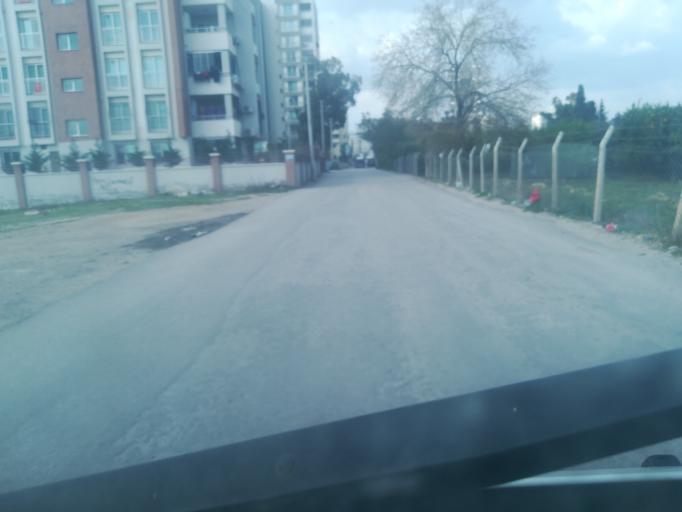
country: TR
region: Adana
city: Seyhan
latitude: 37.0066
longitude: 35.2701
